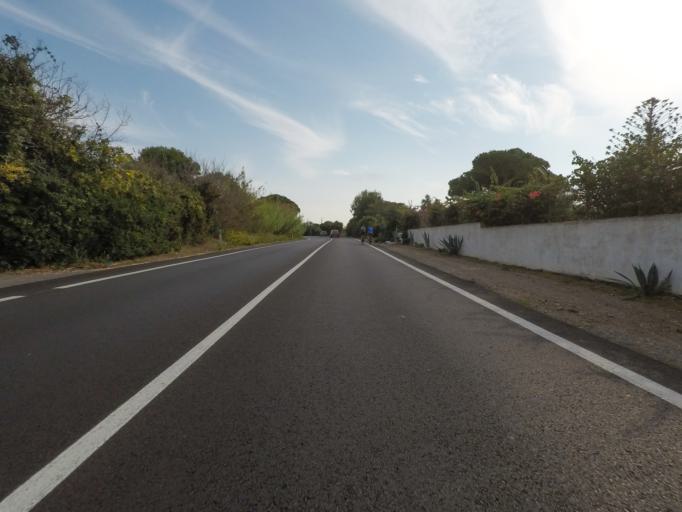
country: IT
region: Latium
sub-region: Citta metropolitana di Roma Capitale
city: Civitavecchia
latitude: 42.0495
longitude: 11.8207
